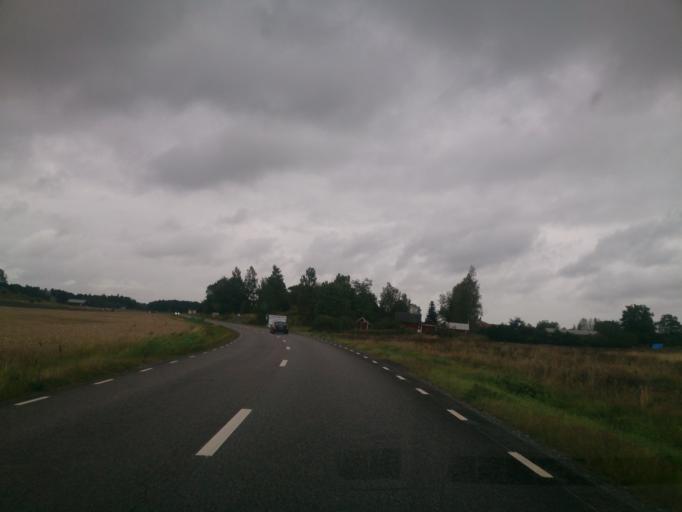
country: SE
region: OEstergoetland
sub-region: Norrkopings Kommun
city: Krokek
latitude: 58.5586
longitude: 16.6061
